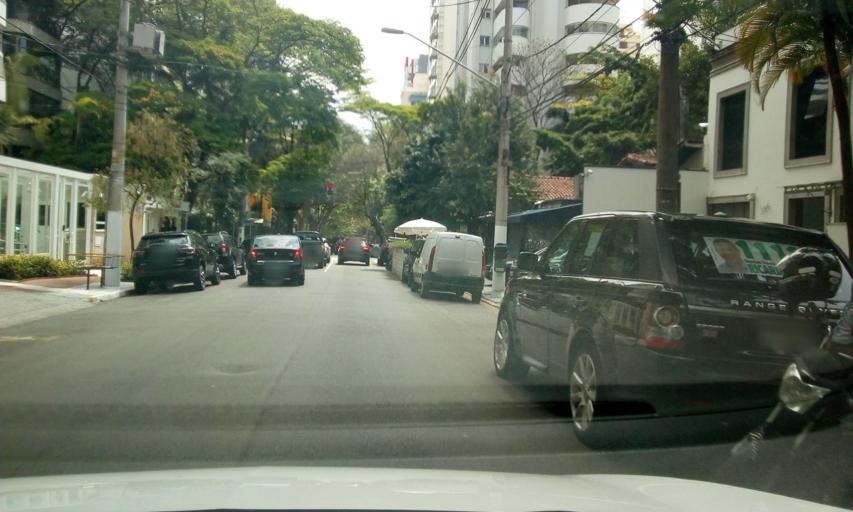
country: BR
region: Sao Paulo
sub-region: Sao Paulo
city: Sao Paulo
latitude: -23.5942
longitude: -46.6699
